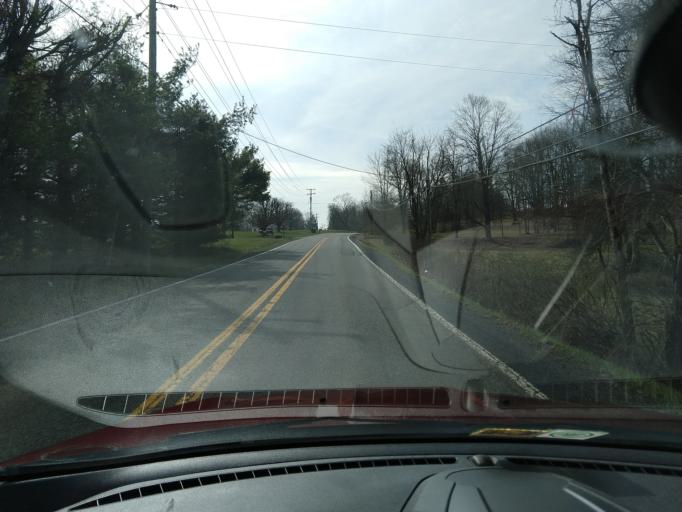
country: US
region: West Virginia
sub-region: Greenbrier County
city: Lewisburg
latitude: 37.8707
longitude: -80.4110
